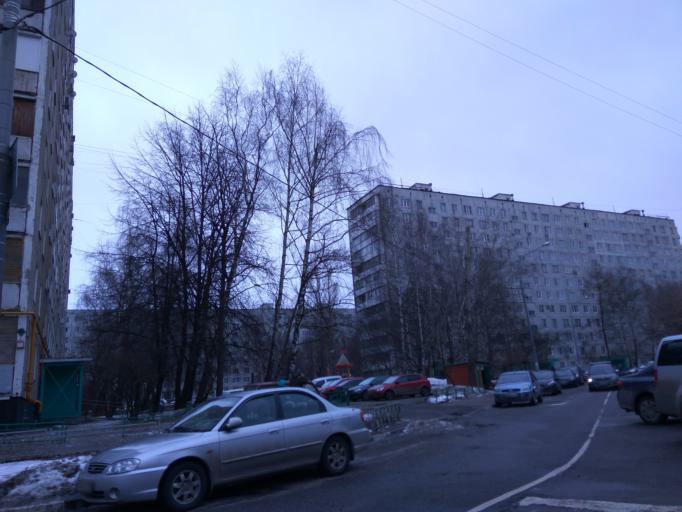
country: RU
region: Moscow
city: Biryulevo
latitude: 55.5958
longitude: 37.6655
